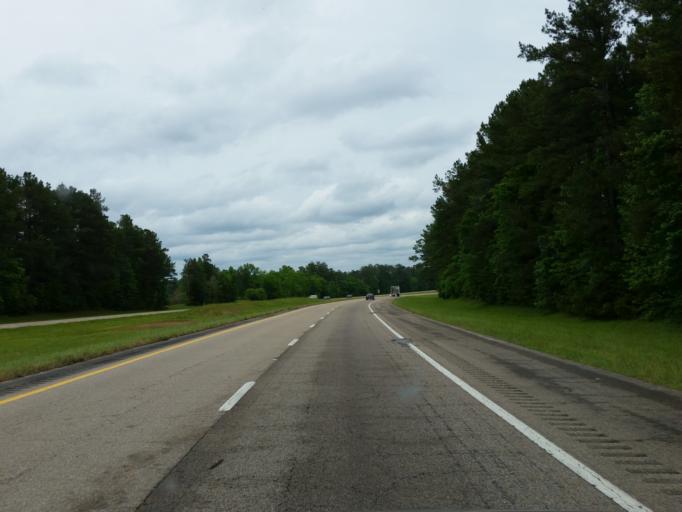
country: US
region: Mississippi
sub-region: Clarke County
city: Stonewall
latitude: 32.0430
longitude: -88.9201
